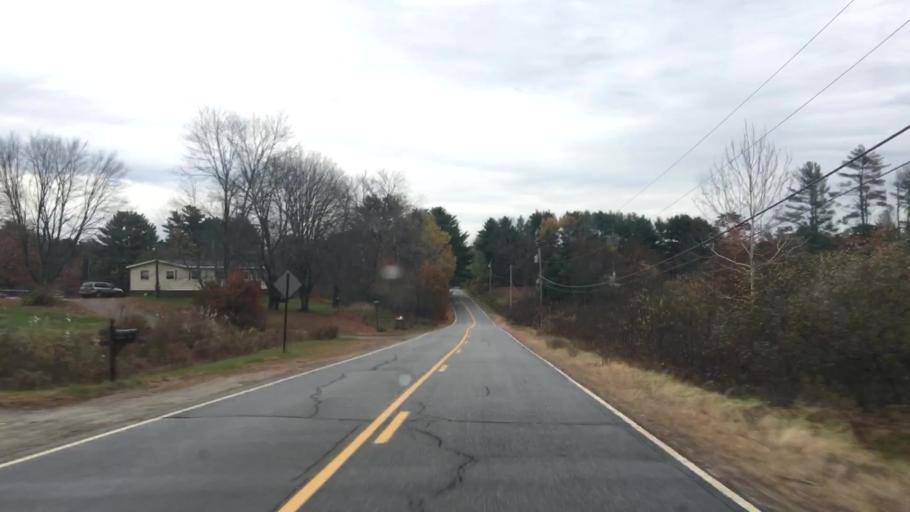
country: US
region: Maine
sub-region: Lincoln County
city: Whitefield
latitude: 44.1651
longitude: -69.6484
